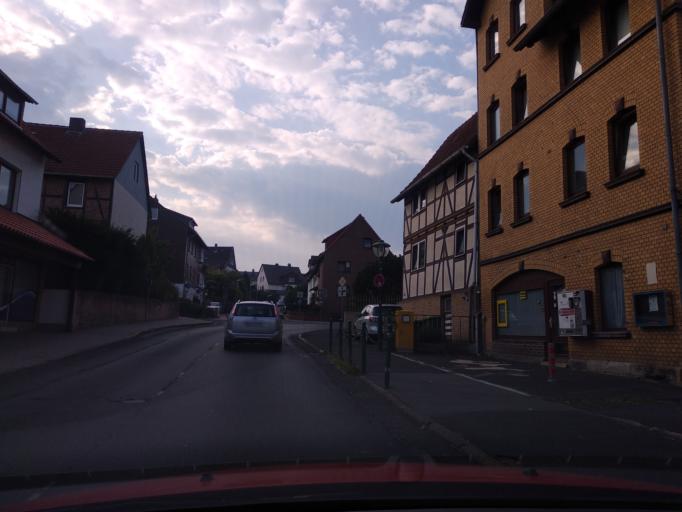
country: DE
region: Hesse
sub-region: Regierungsbezirk Kassel
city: Calden
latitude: 51.3657
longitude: 9.3928
